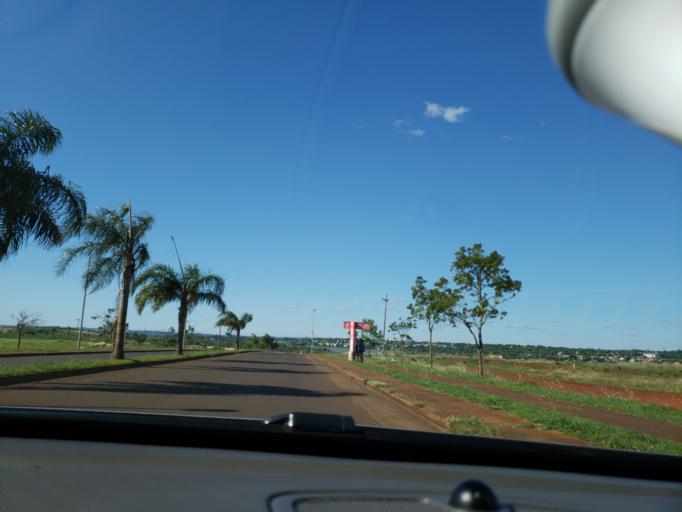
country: AR
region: Misiones
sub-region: Departamento de Capital
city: Posadas
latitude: -27.3916
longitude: -55.9627
